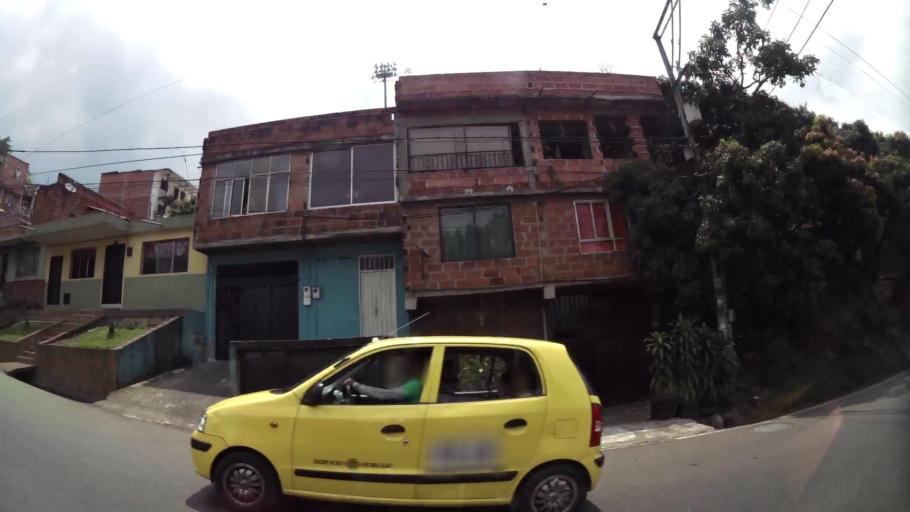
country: CO
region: Antioquia
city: Medellin
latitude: 6.2623
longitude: -75.5547
